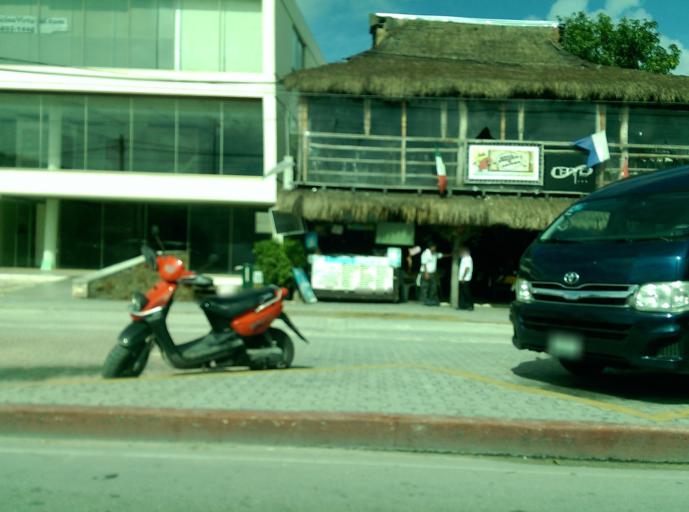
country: MX
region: Quintana Roo
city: Tulum
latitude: 20.2114
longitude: -87.4621
